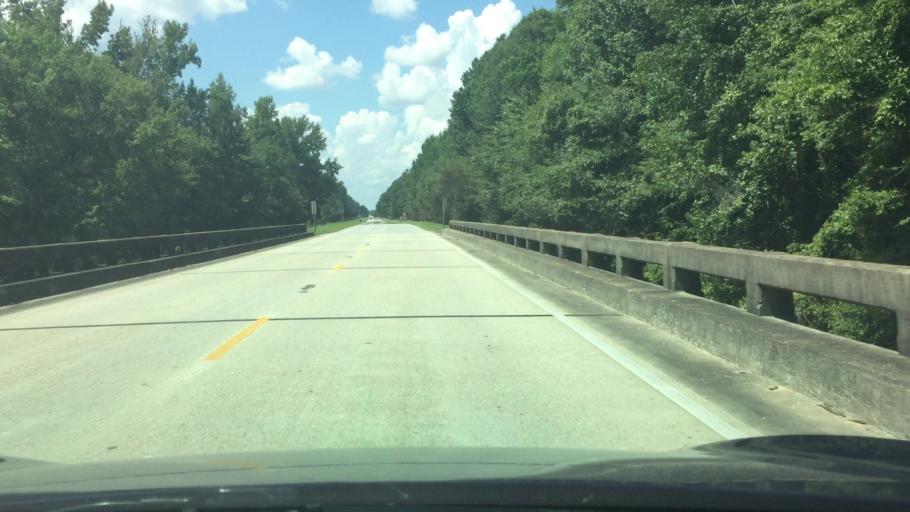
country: US
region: Alabama
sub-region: Elmore County
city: Tallassee
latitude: 32.3930
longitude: -85.9756
